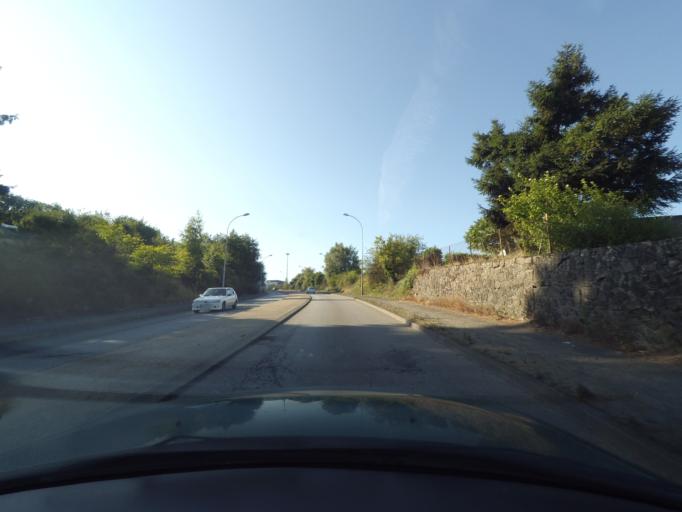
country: FR
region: Poitou-Charentes
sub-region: Departement des Deux-Sevres
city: Chatillon-sur-Thouet
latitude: 46.6561
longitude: -0.2395
